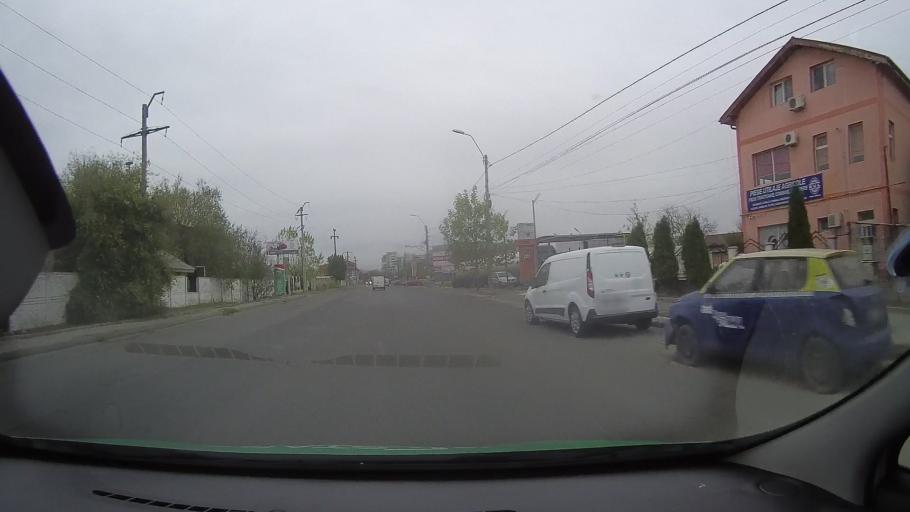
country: RO
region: Ialomita
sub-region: Comuna Slobozia
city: Slobozia
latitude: 44.5725
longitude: 27.3855
